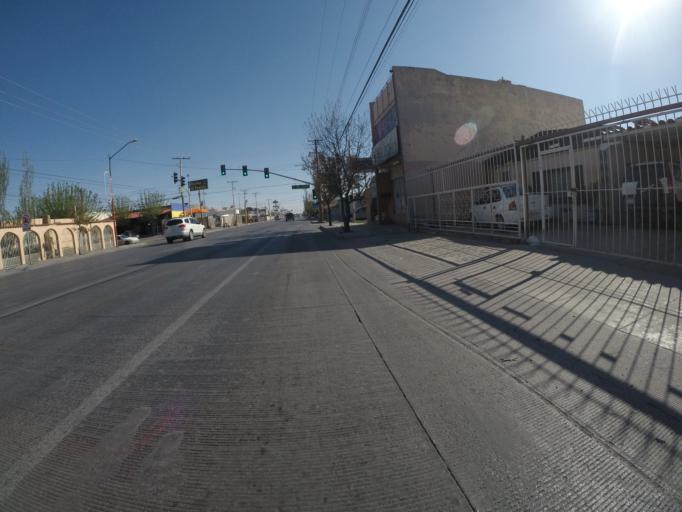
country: MX
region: Chihuahua
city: Ciudad Juarez
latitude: 31.7267
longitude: -106.4505
